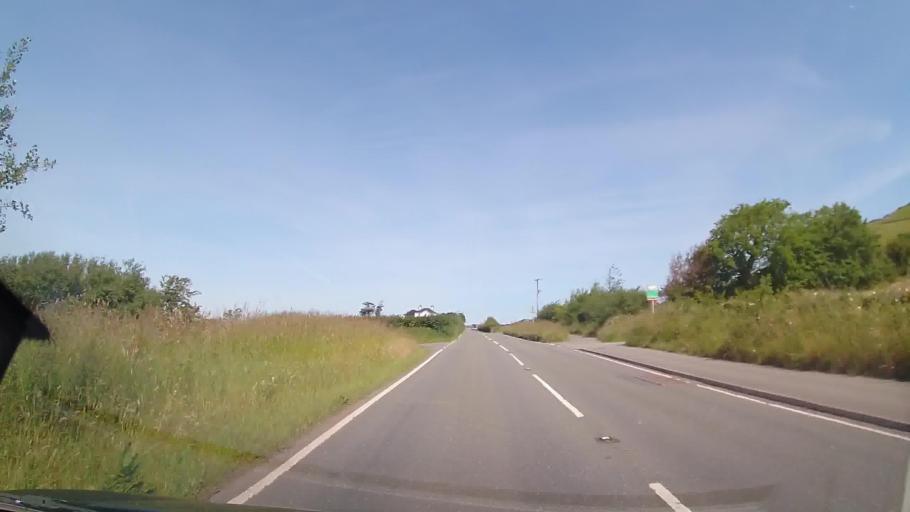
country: GB
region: Wales
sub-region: Gwynedd
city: Tywyn
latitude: 52.5761
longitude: -4.0721
